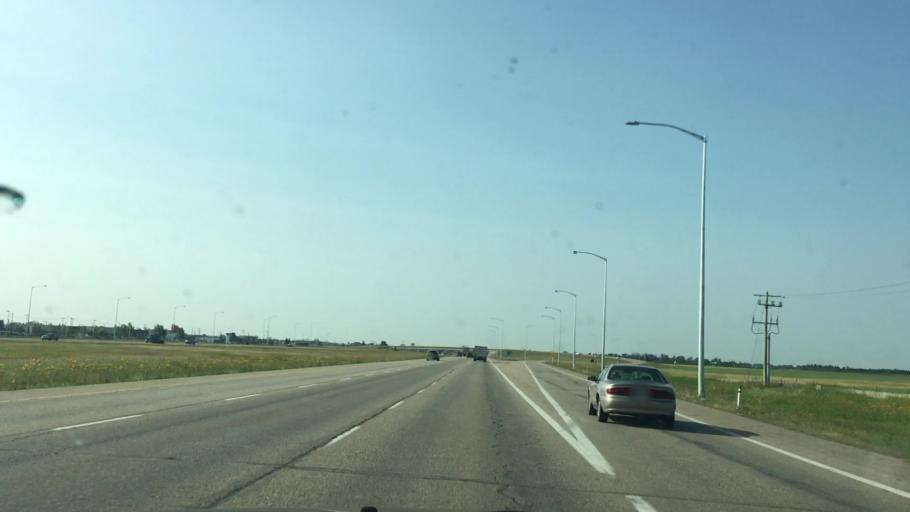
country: CA
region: Alberta
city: Leduc
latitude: 53.2931
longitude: -113.5499
